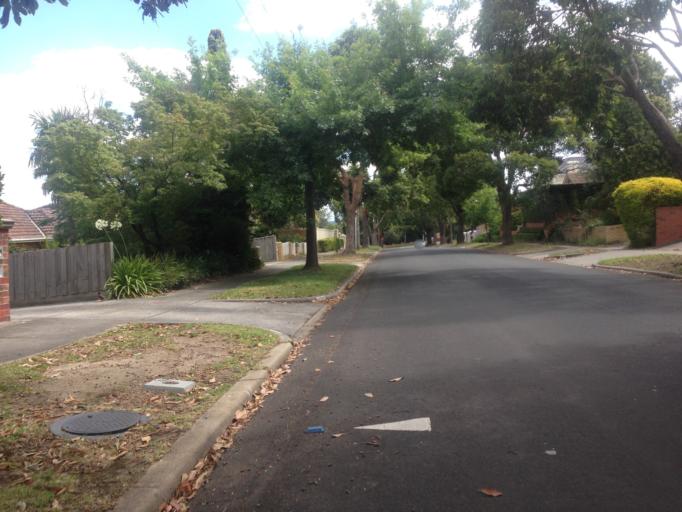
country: AU
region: Victoria
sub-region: Boroondara
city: Balwyn North
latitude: -37.7857
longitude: 145.0796
